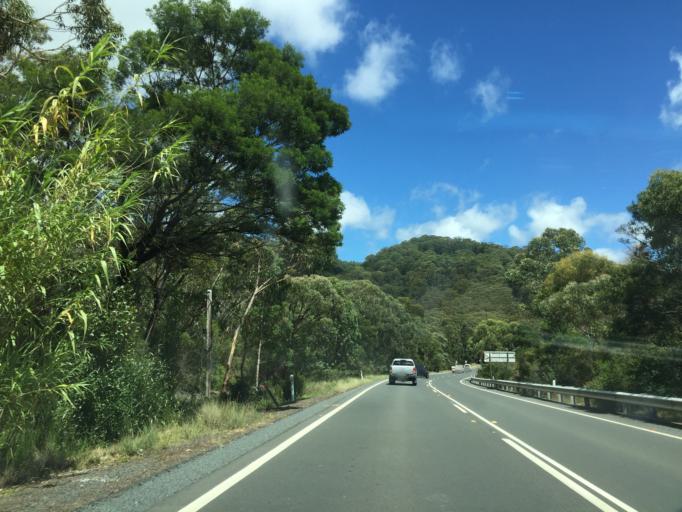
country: AU
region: New South Wales
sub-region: Blue Mountains Municipality
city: Blackheath
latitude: -33.5378
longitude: 150.4353
